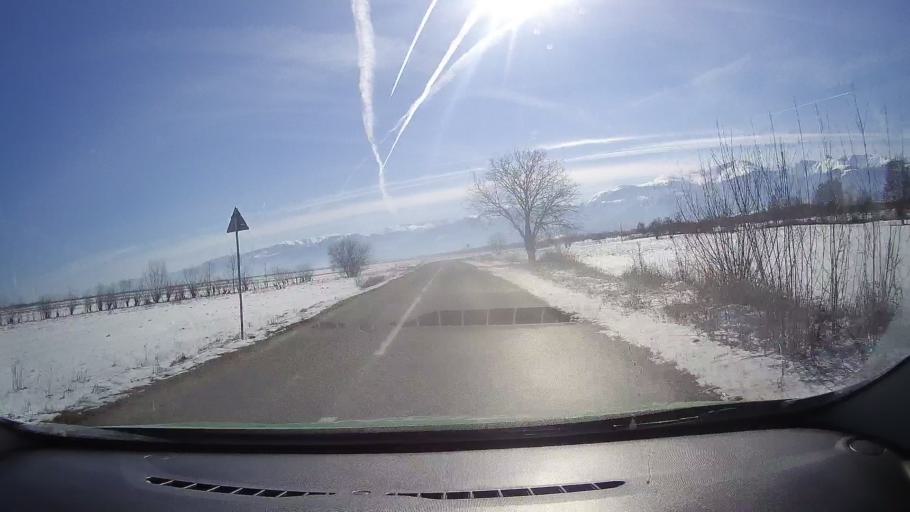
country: RO
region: Brasov
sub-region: Comuna Sambata de Sus
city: Sambata de Sus
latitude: 45.7467
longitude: 24.8421
